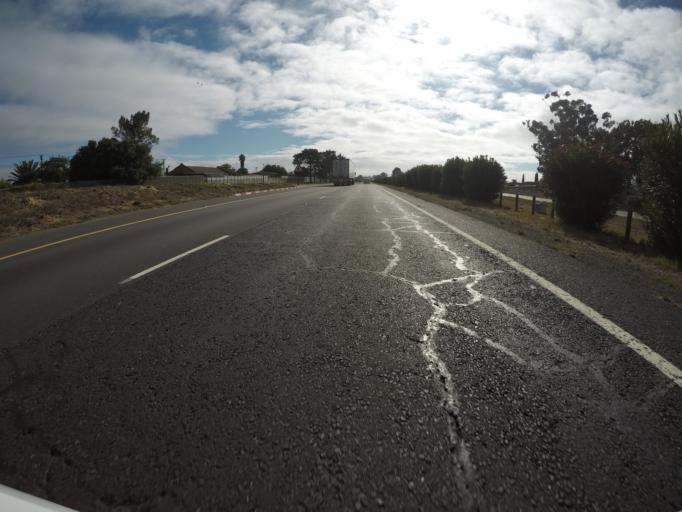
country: ZA
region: Western Cape
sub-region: City of Cape Town
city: Kraaifontein
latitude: -33.8447
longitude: 18.7159
